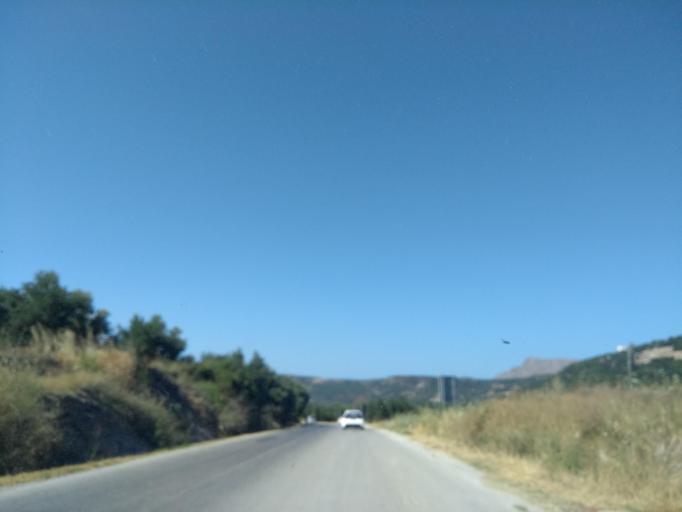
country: GR
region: Crete
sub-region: Nomos Chanias
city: Kissamos
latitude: 35.4356
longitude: 23.6895
